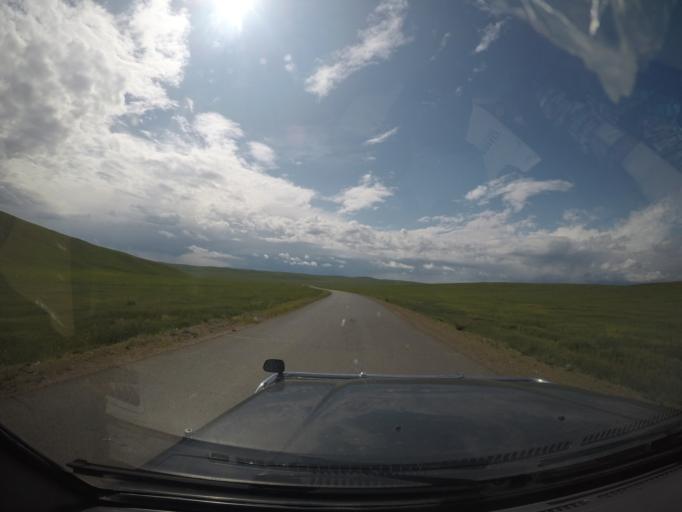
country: MN
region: Hentiy
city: Bayanbulag
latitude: 47.4431
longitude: 109.7484
